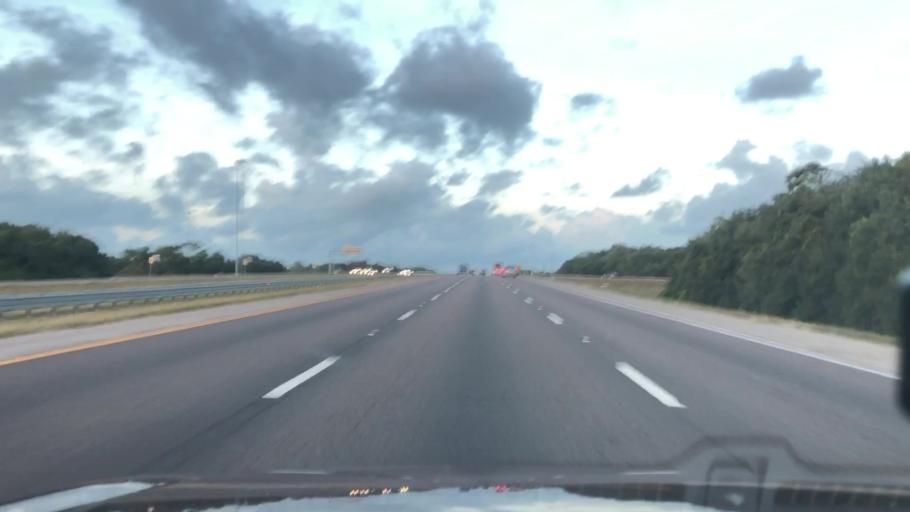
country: US
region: Florida
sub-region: Hillsborough County
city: Apollo Beach
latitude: 27.7885
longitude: -82.3573
